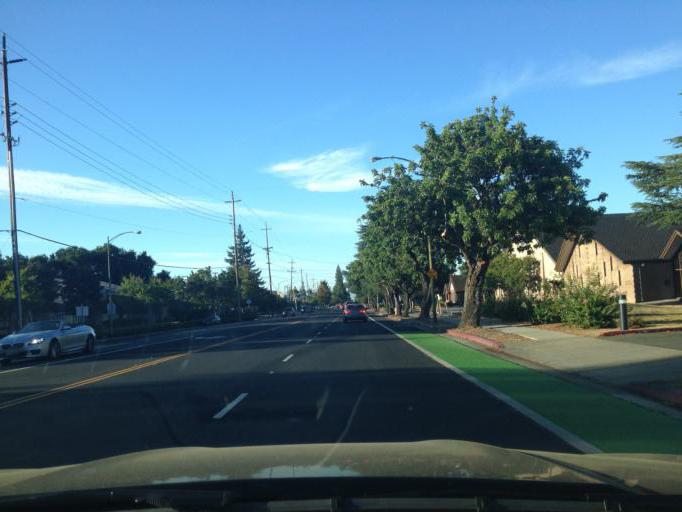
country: US
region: California
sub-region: Santa Clara County
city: Los Gatos
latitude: 37.2308
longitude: -121.9652
